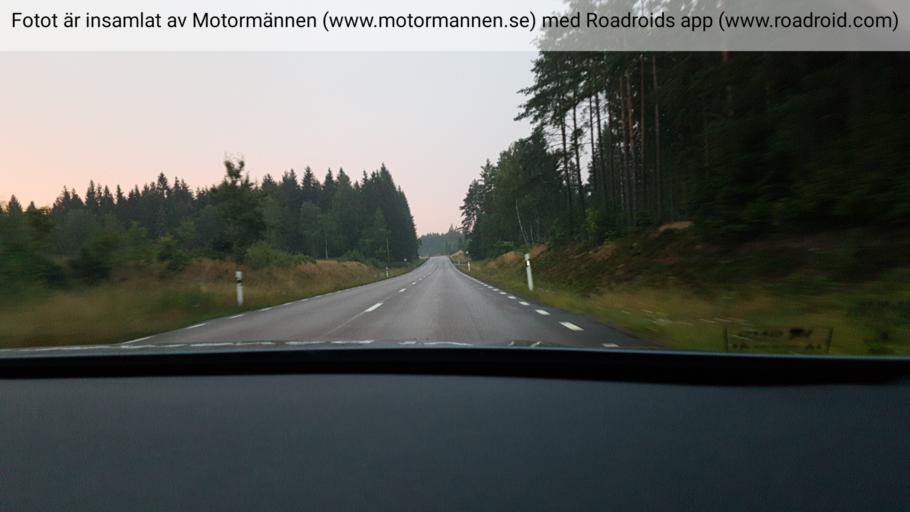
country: SE
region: Vaestra Goetaland
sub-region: Skovde Kommun
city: Skultorp
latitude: 58.2704
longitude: 13.8099
